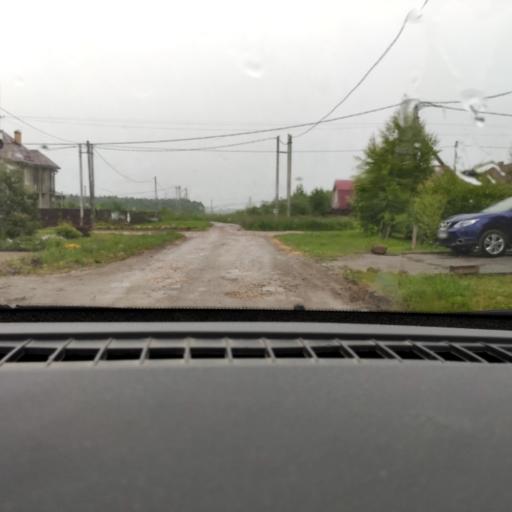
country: RU
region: Perm
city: Perm
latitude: 58.0406
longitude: 56.3725
